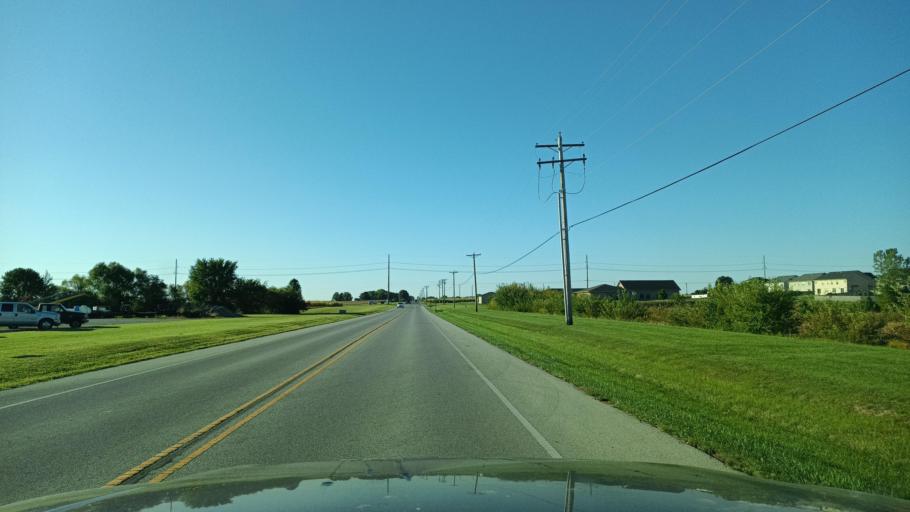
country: US
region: Illinois
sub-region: Champaign County
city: Savoy
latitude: 40.0575
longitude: -88.2384
